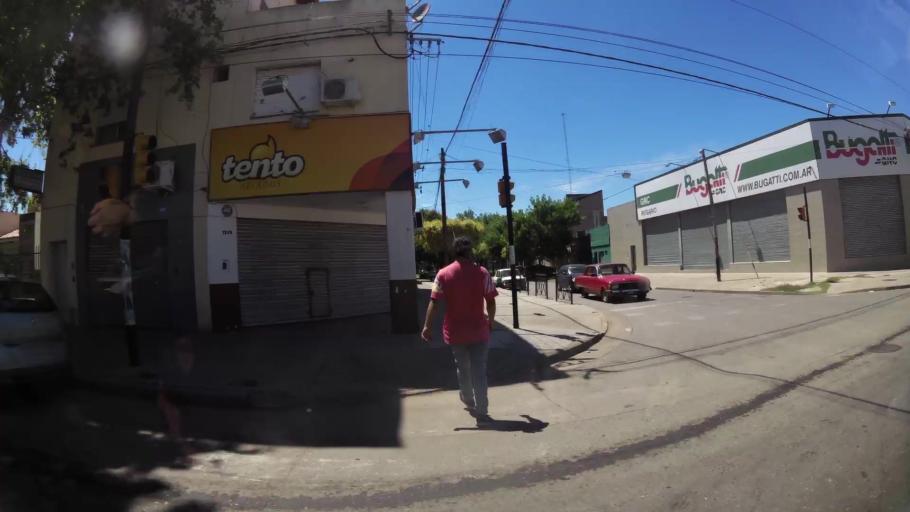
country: AR
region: Santa Fe
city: Perez
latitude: -32.9521
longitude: -60.7119
